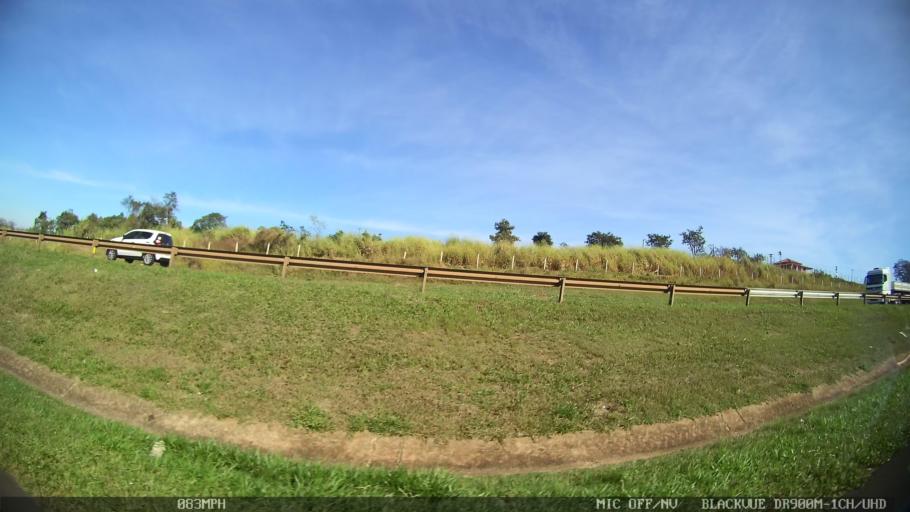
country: BR
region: Sao Paulo
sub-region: Pirassununga
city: Pirassununga
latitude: -22.0897
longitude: -47.4189
